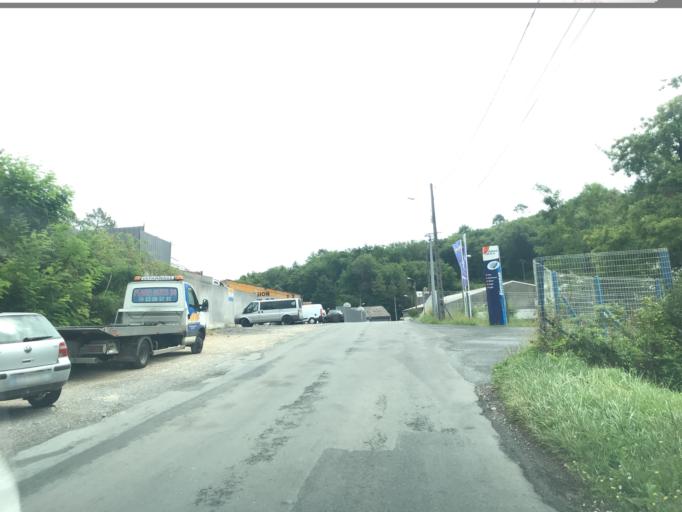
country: FR
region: Aquitaine
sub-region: Departement de la Dordogne
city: Chancelade
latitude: 45.1825
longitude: 0.6669
